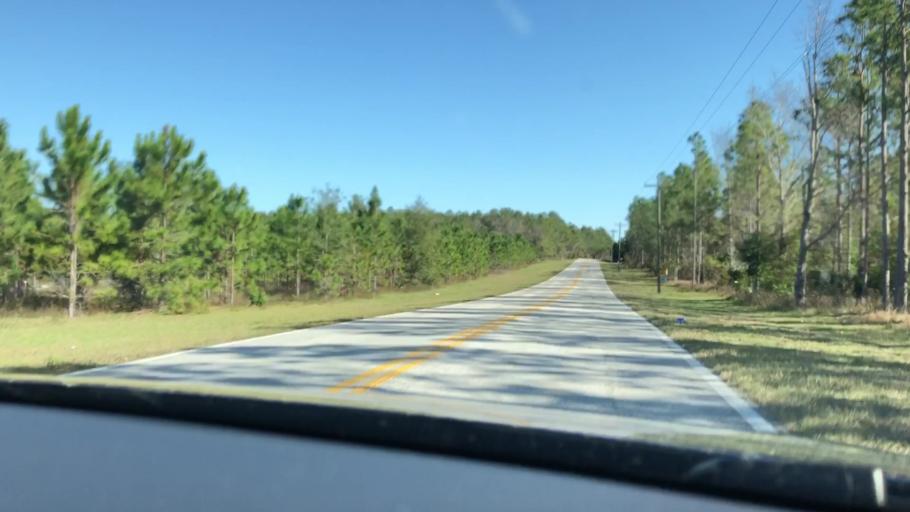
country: US
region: Florida
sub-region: Lake County
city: Eustis
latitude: 28.8728
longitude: -81.6248
